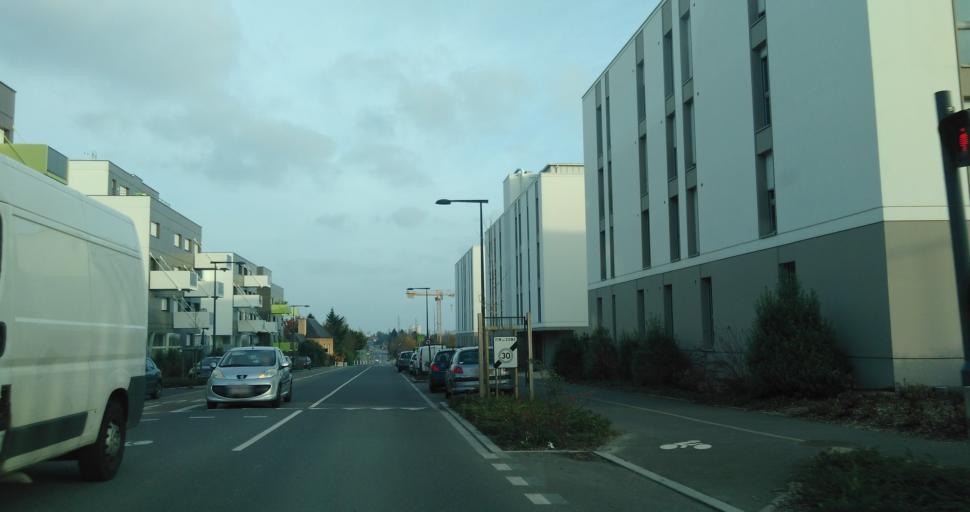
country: FR
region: Brittany
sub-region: Departement d'Ille-et-Vilaine
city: Vezin-le-Coquet
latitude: 48.1189
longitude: -1.7489
